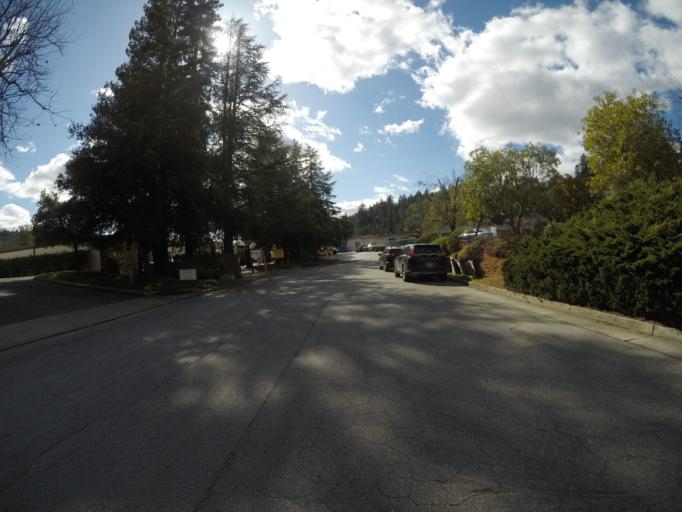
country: US
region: California
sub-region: Santa Cruz County
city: Scotts Valley
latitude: 37.0589
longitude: -122.0087
